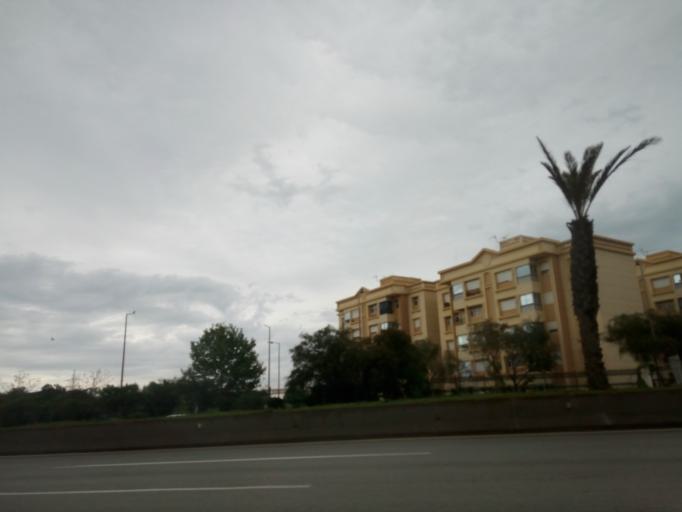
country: DZ
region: Tipaza
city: Cheraga
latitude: 36.7488
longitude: 2.9406
